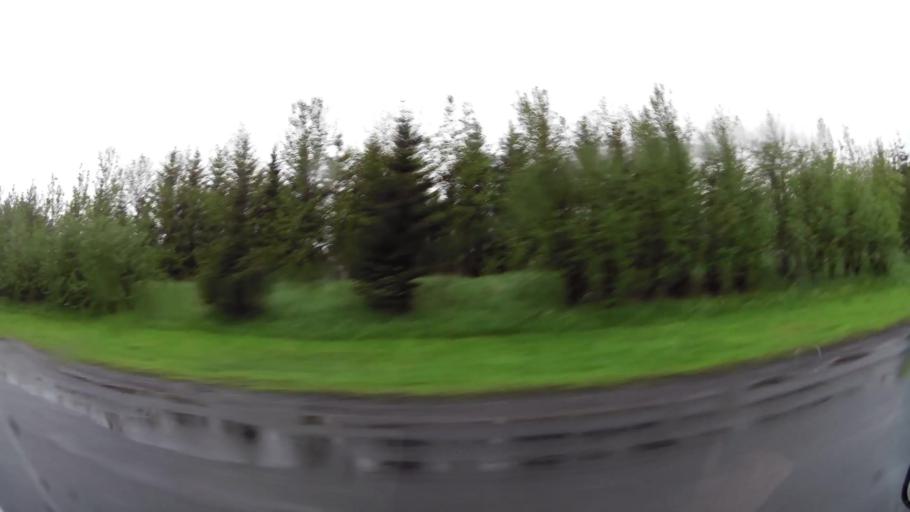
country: IS
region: South
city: Selfoss
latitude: 63.9359
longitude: -20.9790
